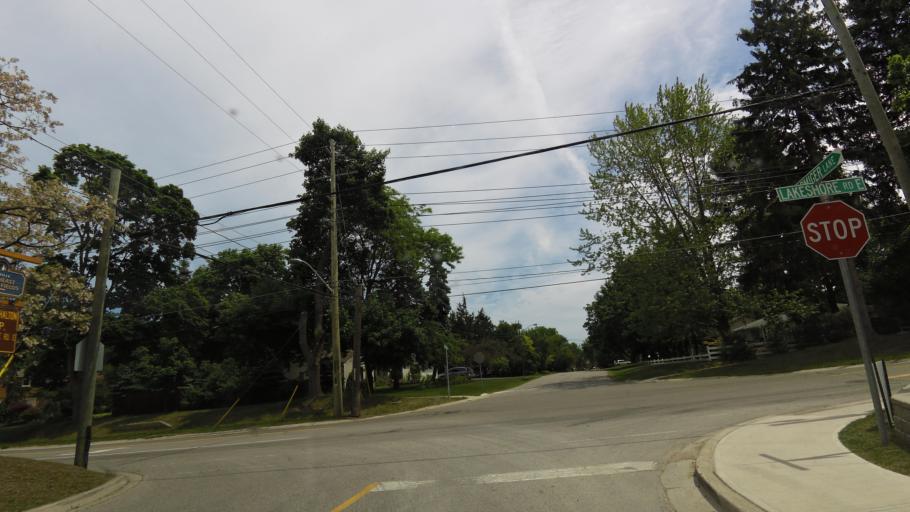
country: CA
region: Ontario
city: Oakville
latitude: 43.4814
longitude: -79.6299
